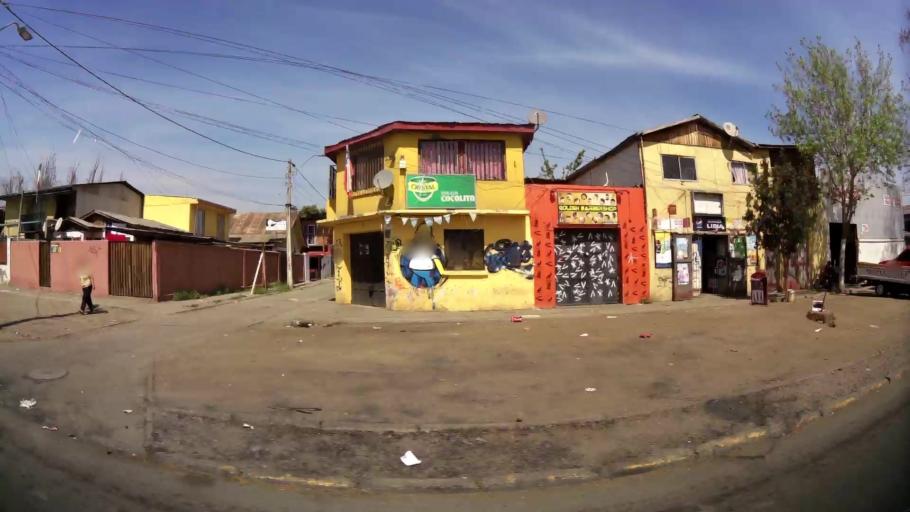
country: CL
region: Santiago Metropolitan
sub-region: Provincia de Santiago
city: Lo Prado
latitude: -33.4231
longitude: -70.7372
